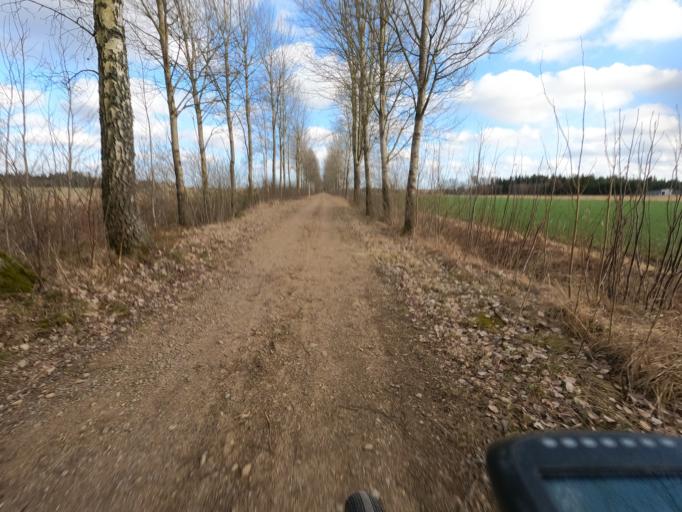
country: SE
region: Kronoberg
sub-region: Alvesta Kommun
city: Vislanda
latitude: 56.7319
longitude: 14.5553
